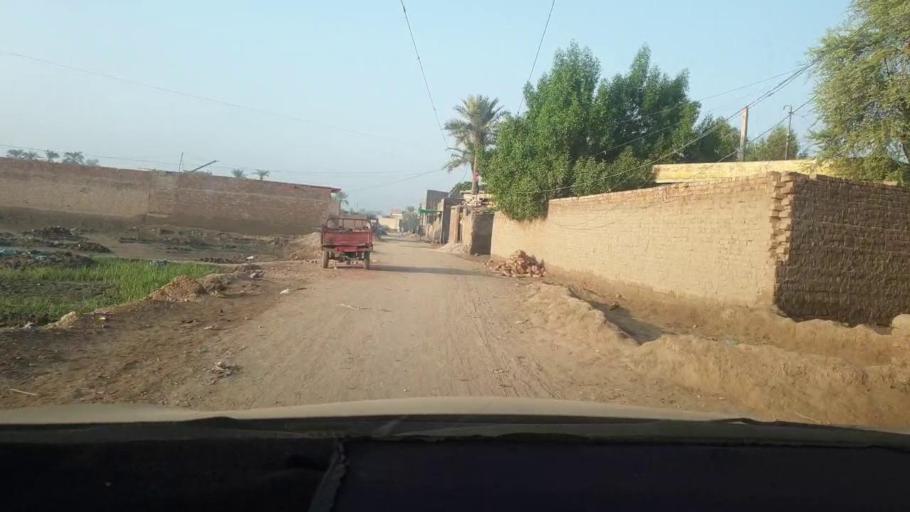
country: PK
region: Sindh
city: Larkana
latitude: 27.5480
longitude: 68.2308
